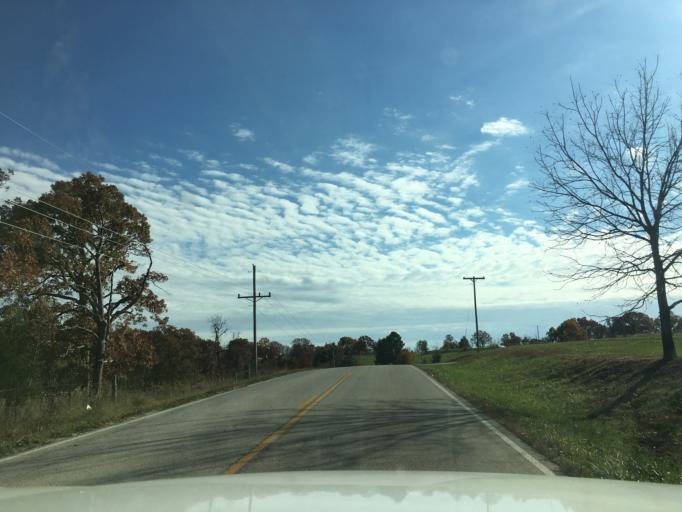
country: US
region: Missouri
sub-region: Maries County
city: Belle
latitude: 38.3281
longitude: -91.7610
